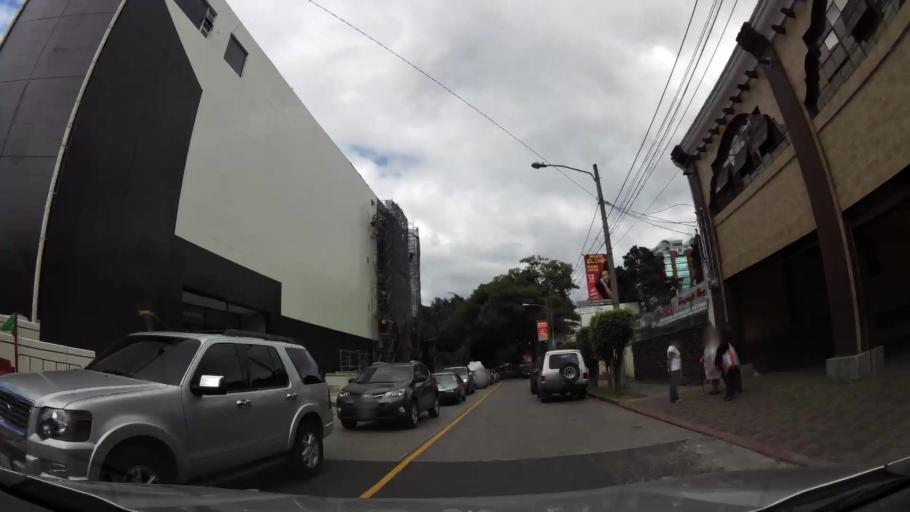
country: GT
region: Guatemala
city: Santa Catarina Pinula
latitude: 14.5939
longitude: -90.5147
